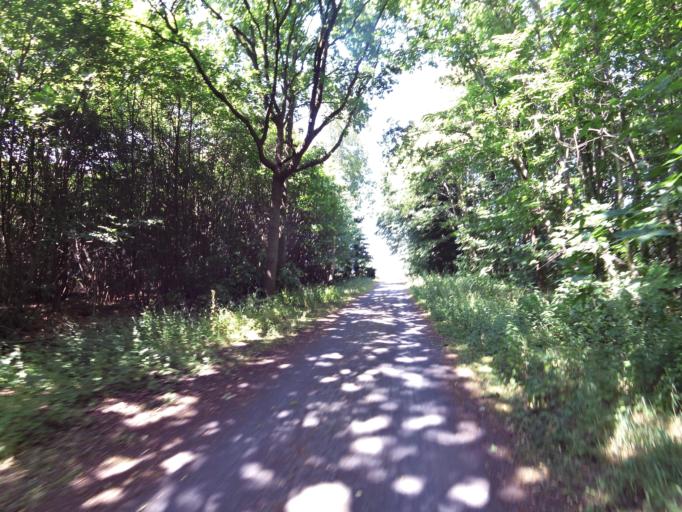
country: BE
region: Flanders
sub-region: Provincie West-Vlaanderen
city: Zedelgem
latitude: 51.1919
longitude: 3.1611
